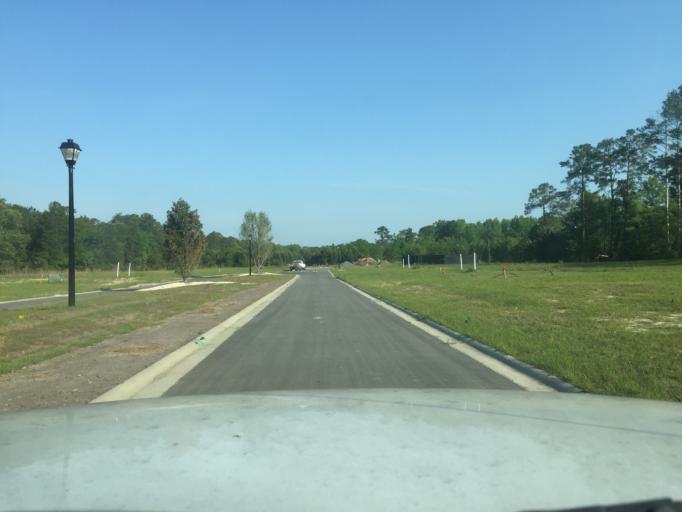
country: US
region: Georgia
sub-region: Chatham County
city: Georgetown
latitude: 32.0390
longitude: -81.2227
